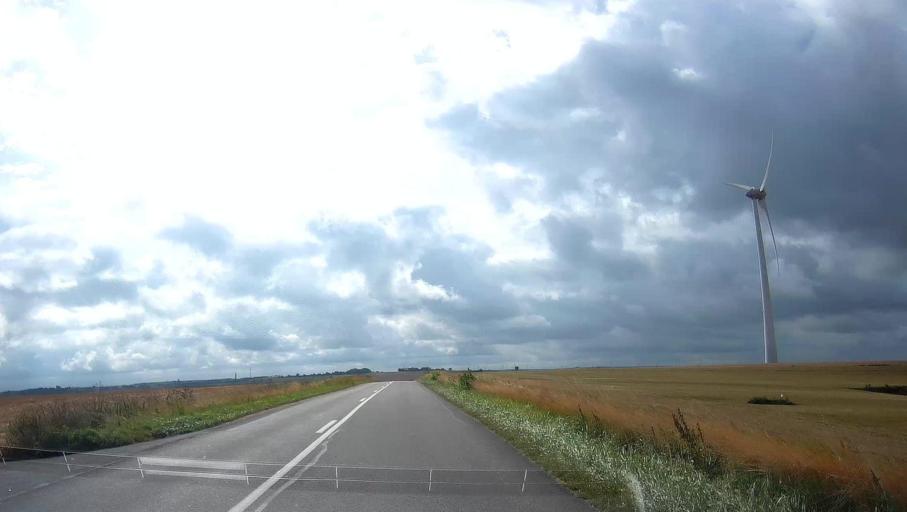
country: FR
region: Champagne-Ardenne
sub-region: Departement des Ardennes
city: Rethel
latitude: 49.5291
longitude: 4.3340
